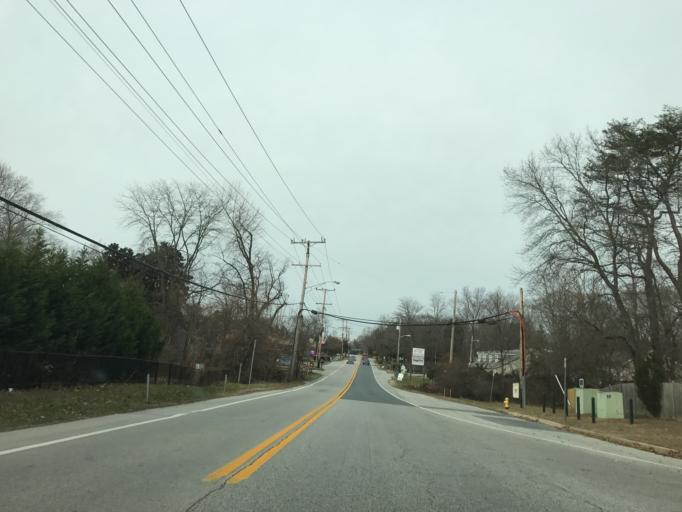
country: US
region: Maryland
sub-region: Anne Arundel County
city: Pasadena
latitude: 39.1075
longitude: -76.5539
